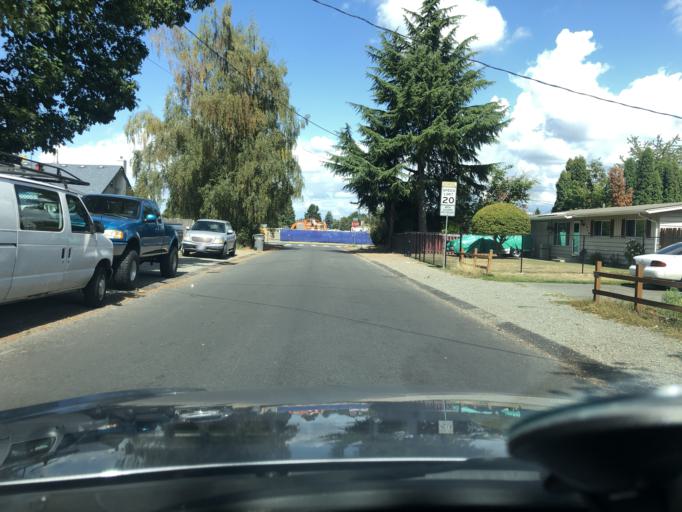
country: US
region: Washington
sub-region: King County
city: Auburn
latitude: 47.3196
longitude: -122.2159
